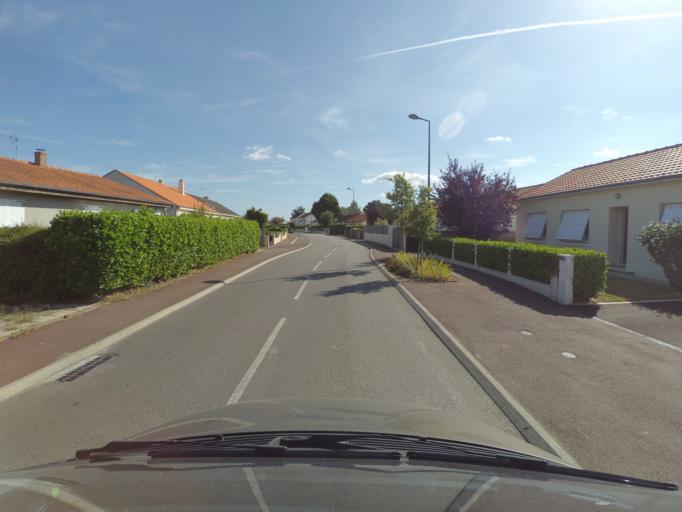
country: FR
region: Pays de la Loire
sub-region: Departement de la Loire-Atlantique
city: Le Bignon
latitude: 47.0984
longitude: -1.4946
